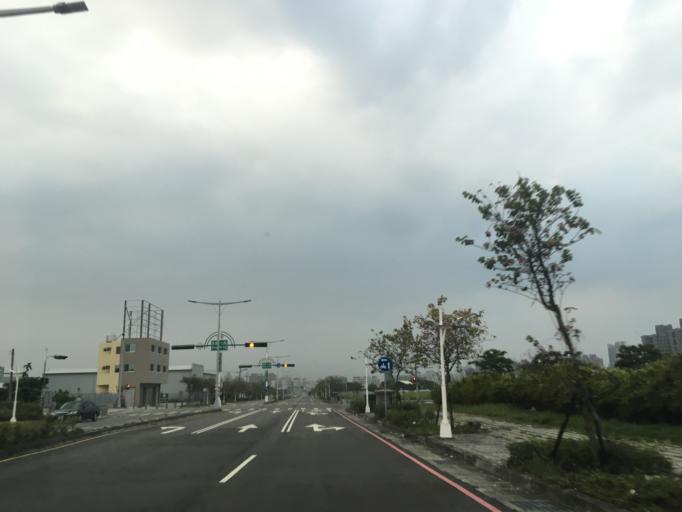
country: TW
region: Taiwan
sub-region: Taichung City
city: Taichung
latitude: 24.1986
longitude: 120.6933
